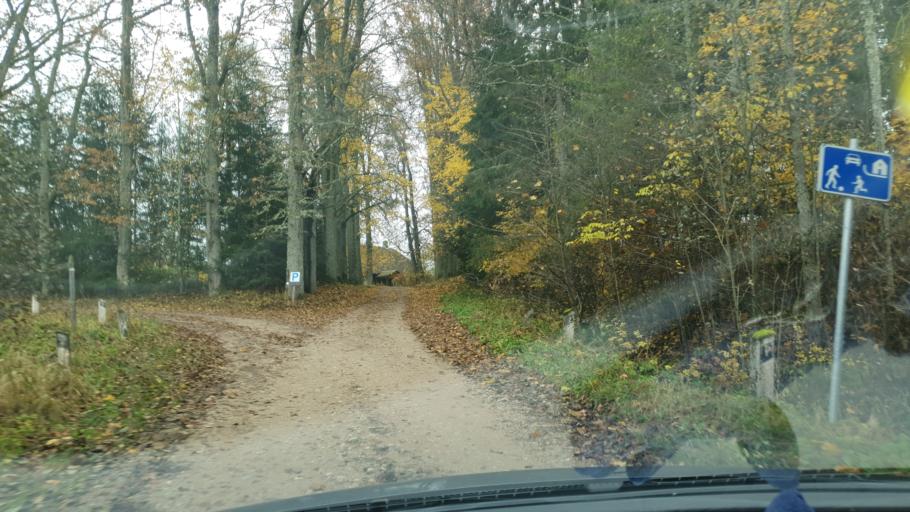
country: EE
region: Viljandimaa
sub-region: Karksi vald
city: Karksi-Nuia
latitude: 58.0034
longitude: 25.5525
